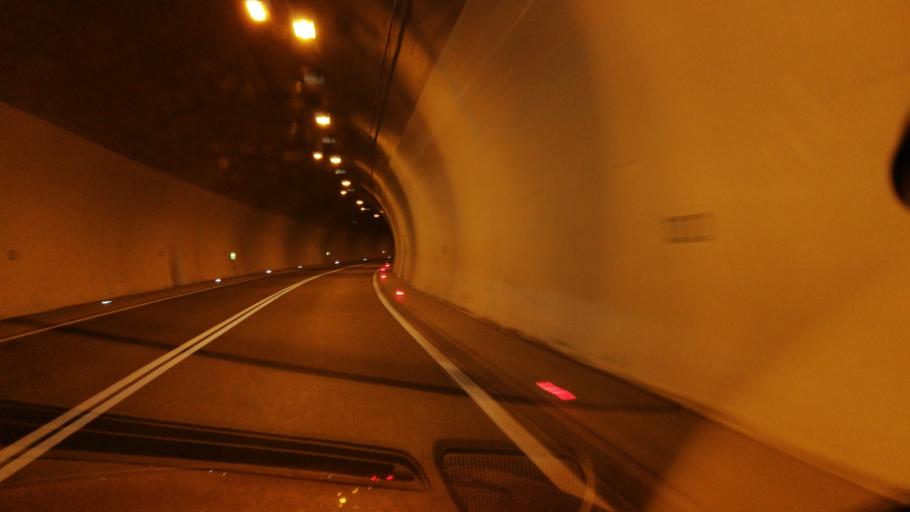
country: AT
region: Upper Austria
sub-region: Politischer Bezirk Steyr-Land
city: Losenstein
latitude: 47.9268
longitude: 14.4318
